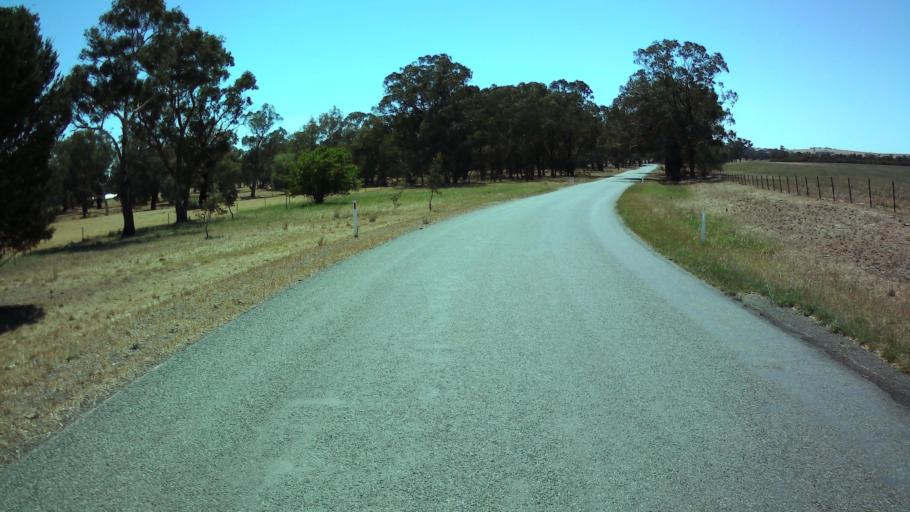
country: AU
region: New South Wales
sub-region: Weddin
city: Grenfell
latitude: -34.0001
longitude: 148.3919
